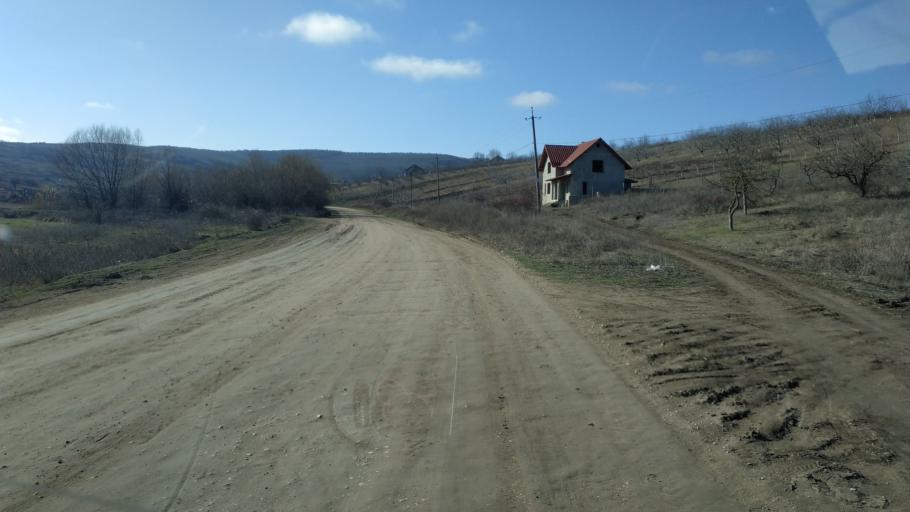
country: MD
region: Hincesti
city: Hincesti
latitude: 46.9280
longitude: 28.6300
